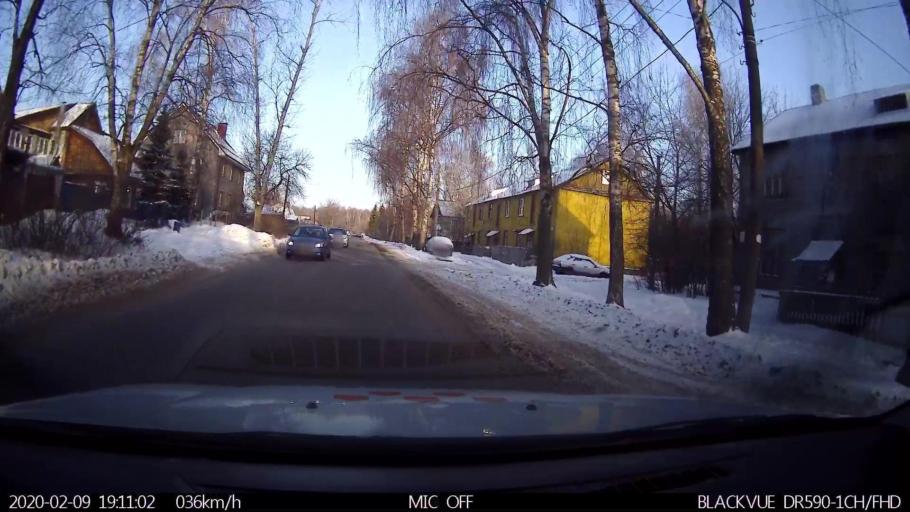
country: RU
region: Nizjnij Novgorod
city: Gorbatovka
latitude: 56.3445
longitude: 43.8288
